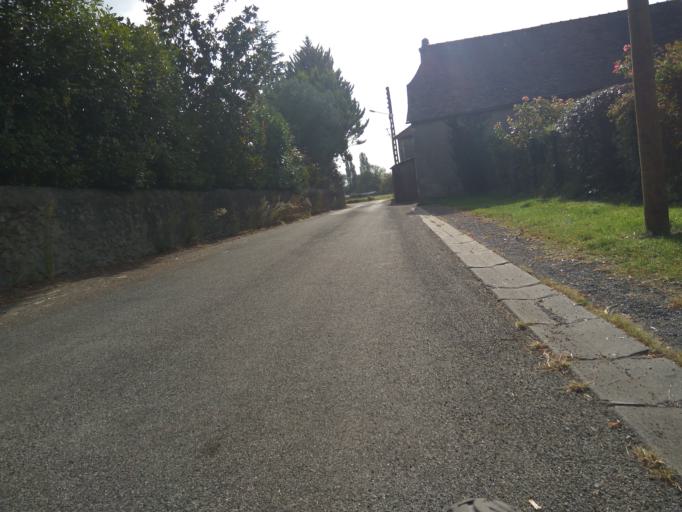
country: FR
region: Aquitaine
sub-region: Departement des Pyrenees-Atlantiques
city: Mazeres-Lezons
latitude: 43.2737
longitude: -0.3506
